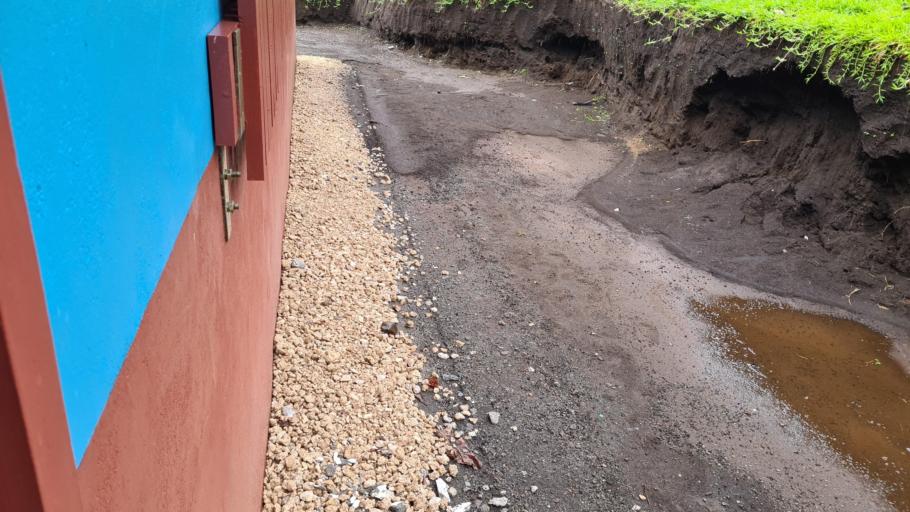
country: VU
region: Malampa
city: Lakatoro
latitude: -16.4649
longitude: 168.2507
